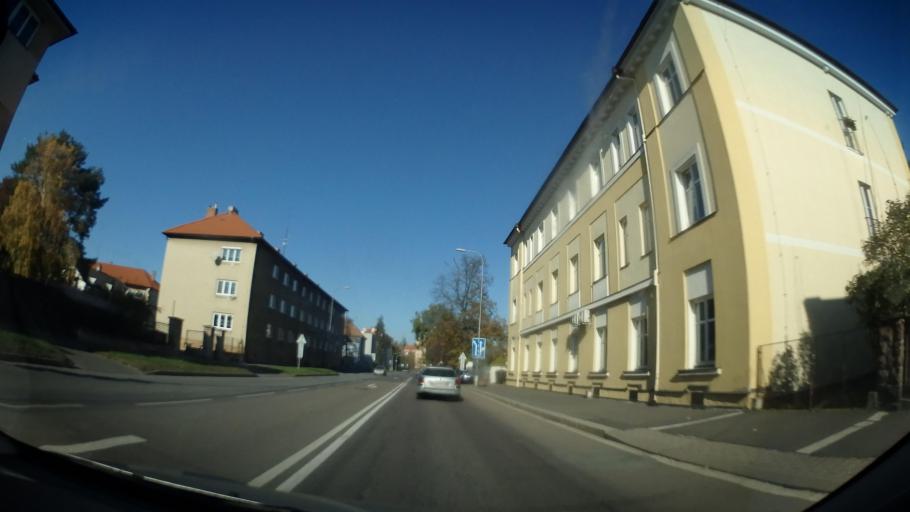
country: CZ
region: Pardubicky
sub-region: Okres Chrudim
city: Chrudim
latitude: 49.9423
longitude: 15.7949
